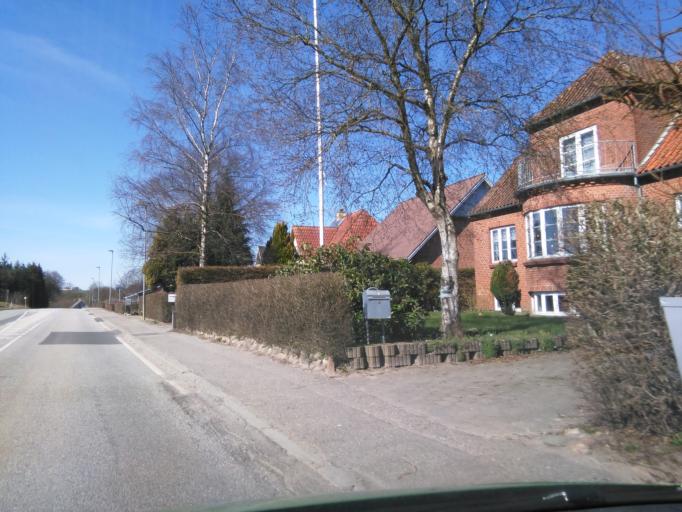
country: DK
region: Central Jutland
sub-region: Horsens Kommune
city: Braedstrup
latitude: 56.0221
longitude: 9.6403
